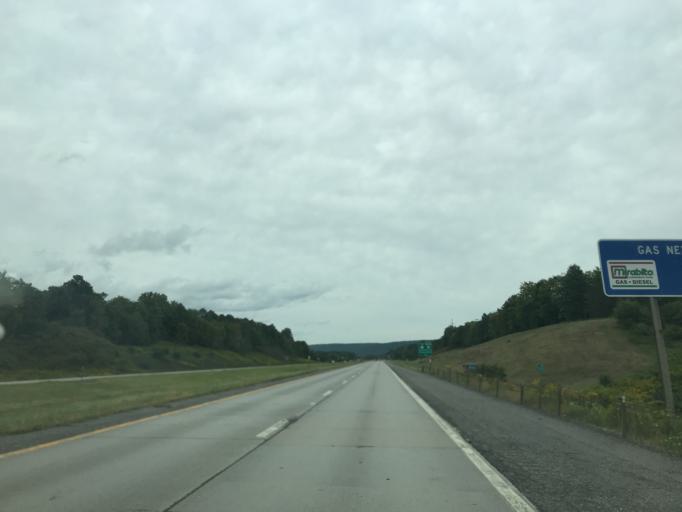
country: US
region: New York
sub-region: Otsego County
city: Oneonta
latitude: 42.4790
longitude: -74.9799
